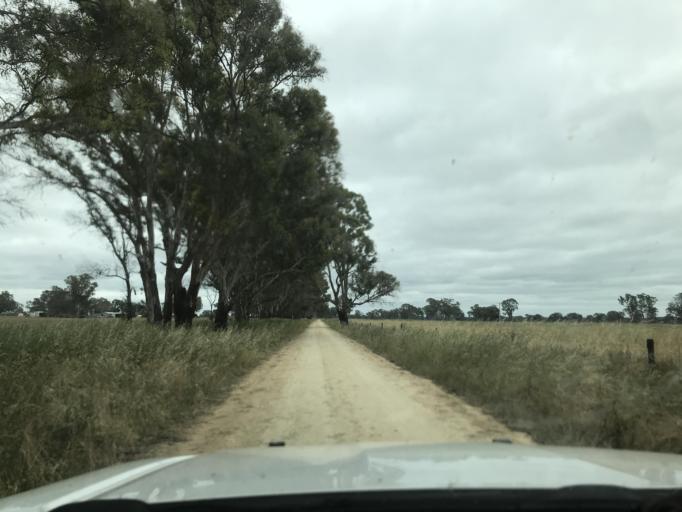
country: AU
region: South Australia
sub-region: Wattle Range
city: Penola
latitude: -37.1800
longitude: 141.0687
